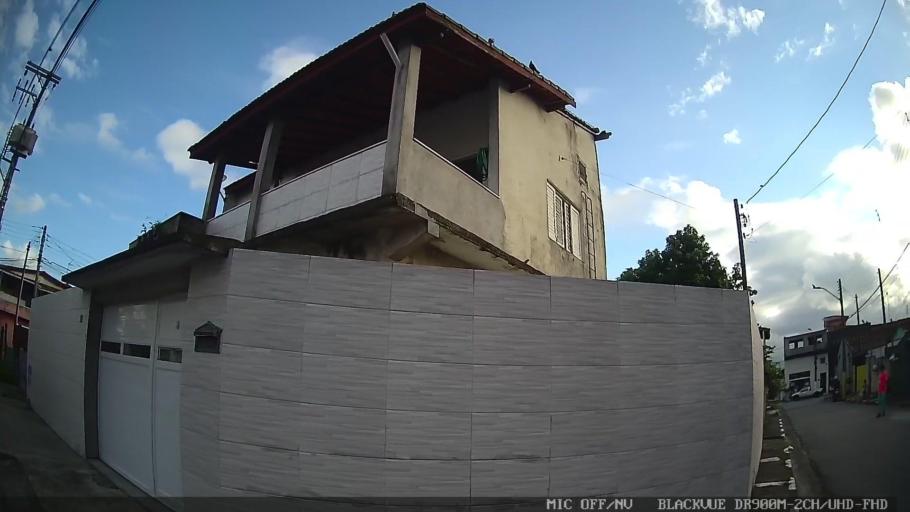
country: BR
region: Sao Paulo
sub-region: Caraguatatuba
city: Caraguatatuba
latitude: -23.6334
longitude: -45.4348
